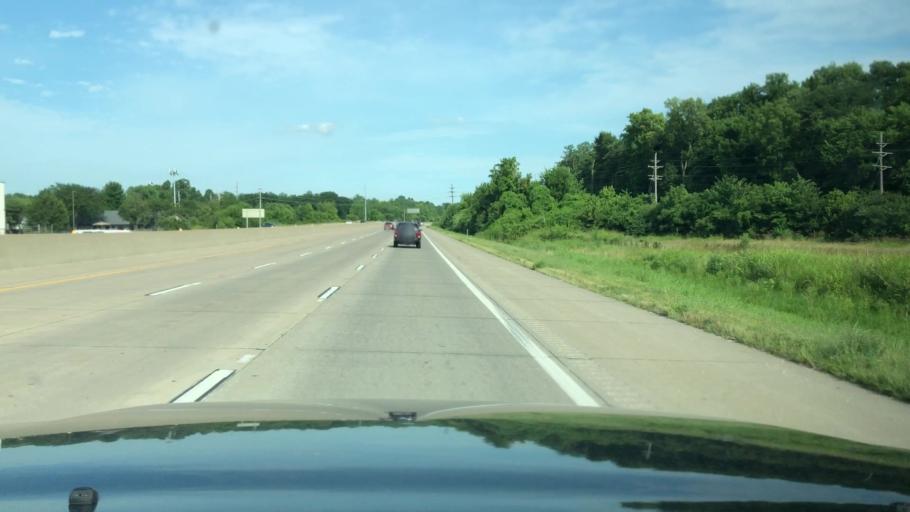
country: US
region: Missouri
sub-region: Saint Charles County
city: Saint Charles
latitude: 38.8195
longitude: -90.5031
